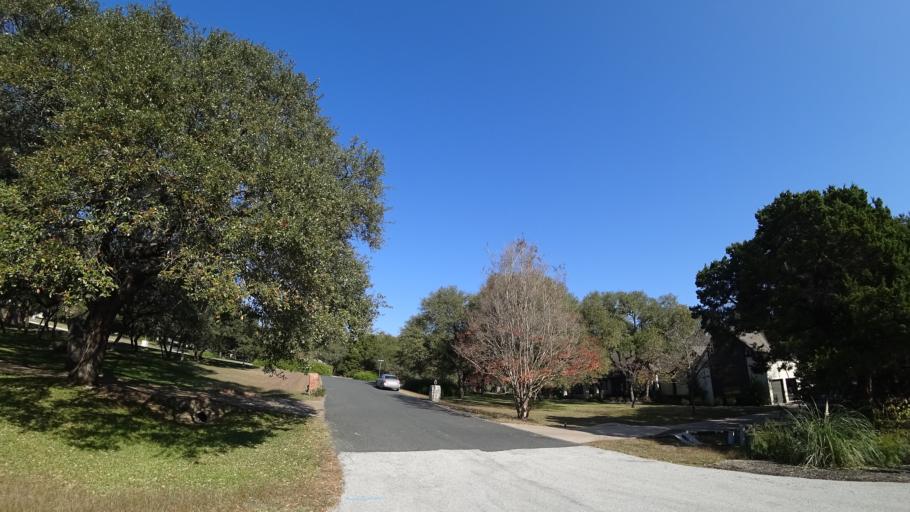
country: US
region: Texas
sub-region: Travis County
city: West Lake Hills
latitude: 30.3704
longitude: -97.8196
